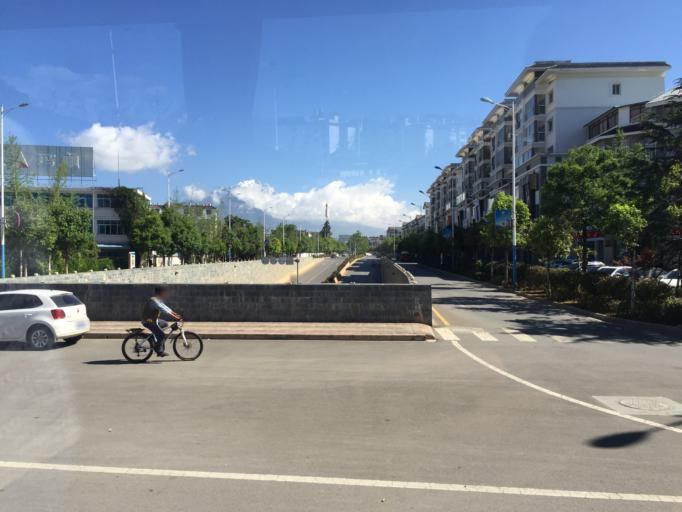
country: CN
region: Yunnan
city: Lijiang
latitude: 26.8813
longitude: 100.2162
